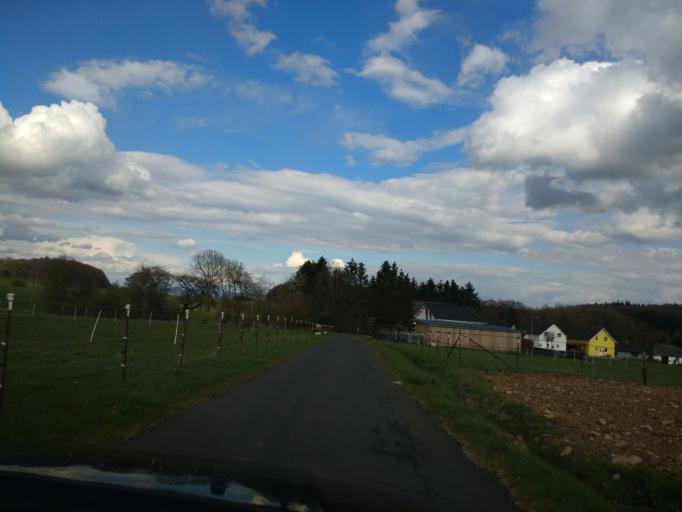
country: DE
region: Rheinland-Pfalz
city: Uxheim
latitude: 50.3259
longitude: 6.7310
